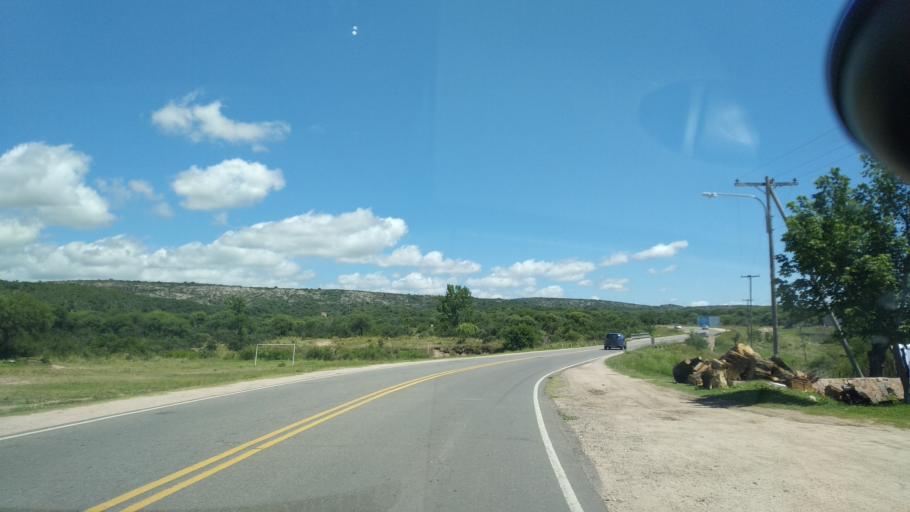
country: AR
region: Cordoba
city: Villa Cura Brochero
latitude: -31.7001
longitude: -65.0370
